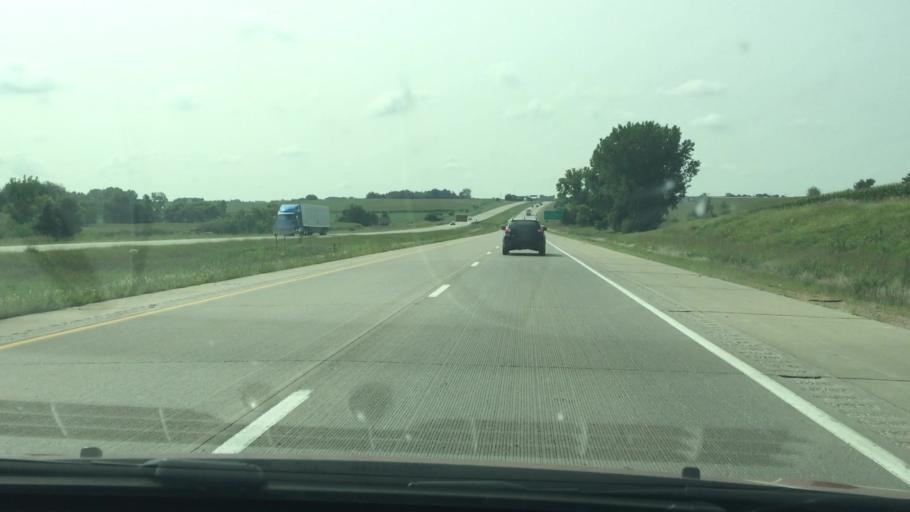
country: US
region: Iowa
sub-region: Scott County
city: Walcott
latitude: 41.5590
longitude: -90.6787
